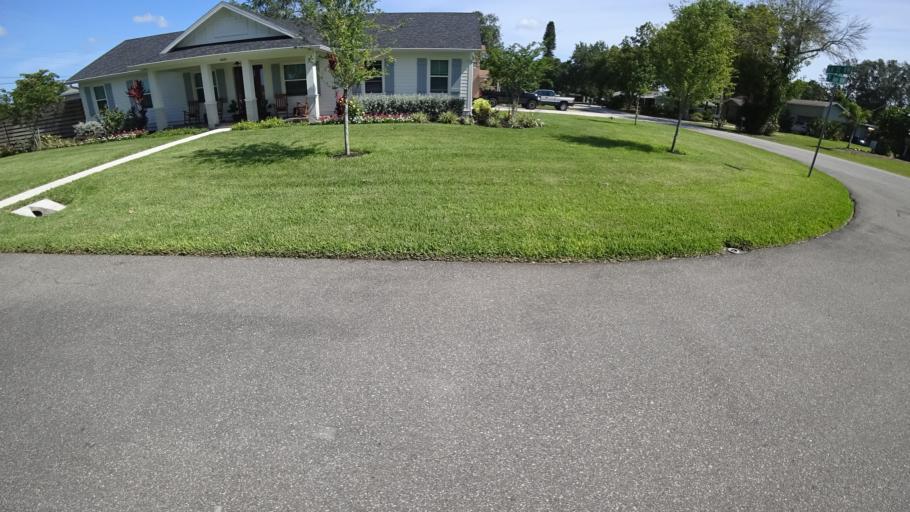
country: US
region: Florida
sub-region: Manatee County
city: West Bradenton
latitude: 27.5073
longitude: -82.6270
